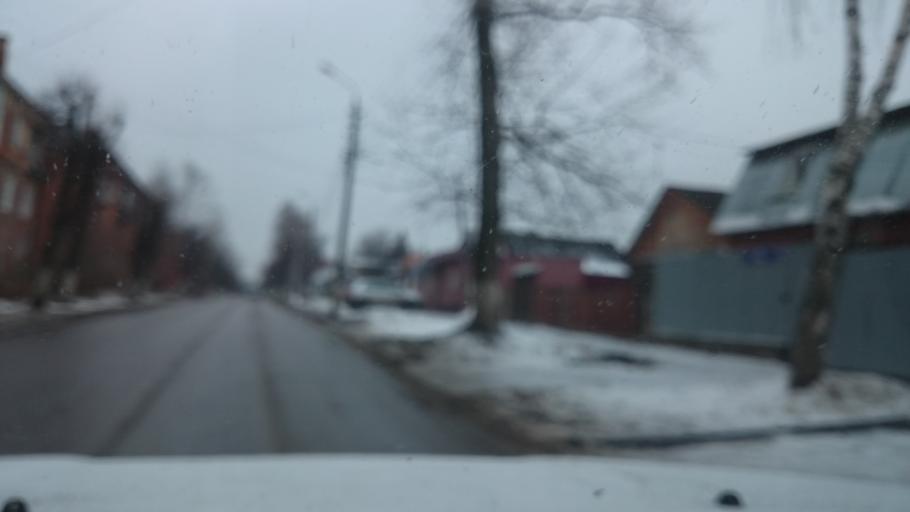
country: RU
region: Tula
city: Mendeleyevskiy
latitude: 54.1732
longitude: 37.5812
